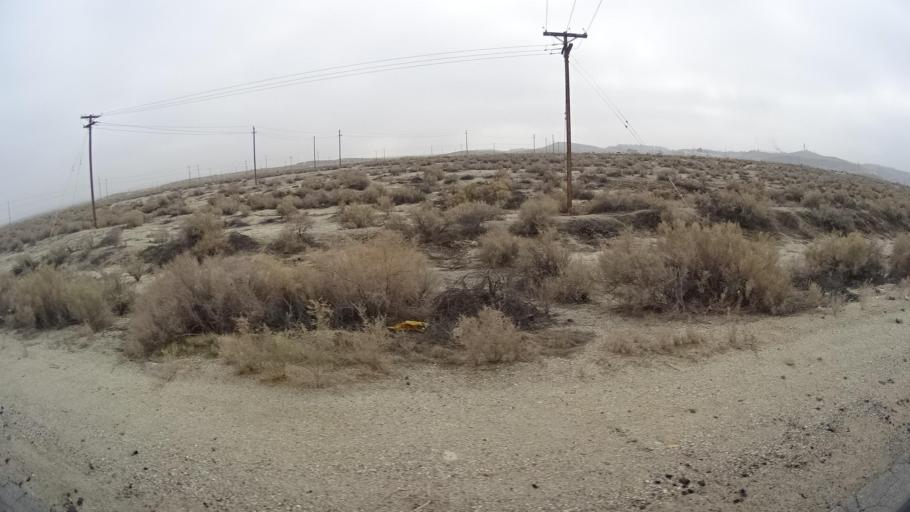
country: US
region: California
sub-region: Kern County
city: Maricopa
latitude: 35.0978
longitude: -119.4058
